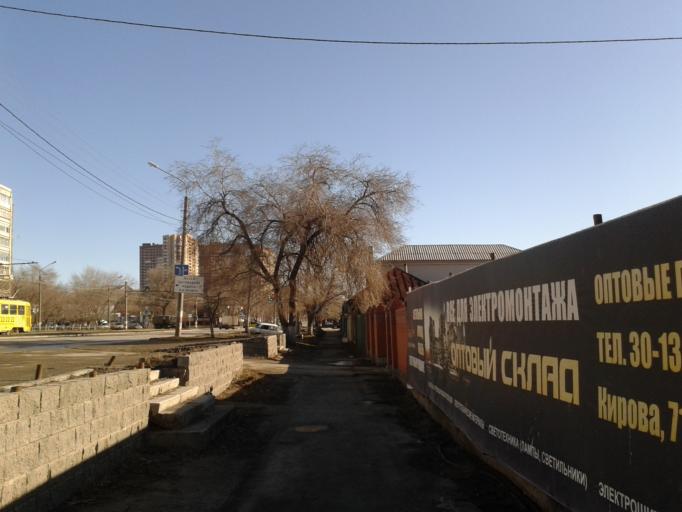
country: RU
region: Ulyanovsk
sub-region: Ulyanovskiy Rayon
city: Ulyanovsk
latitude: 54.2966
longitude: 48.3779
